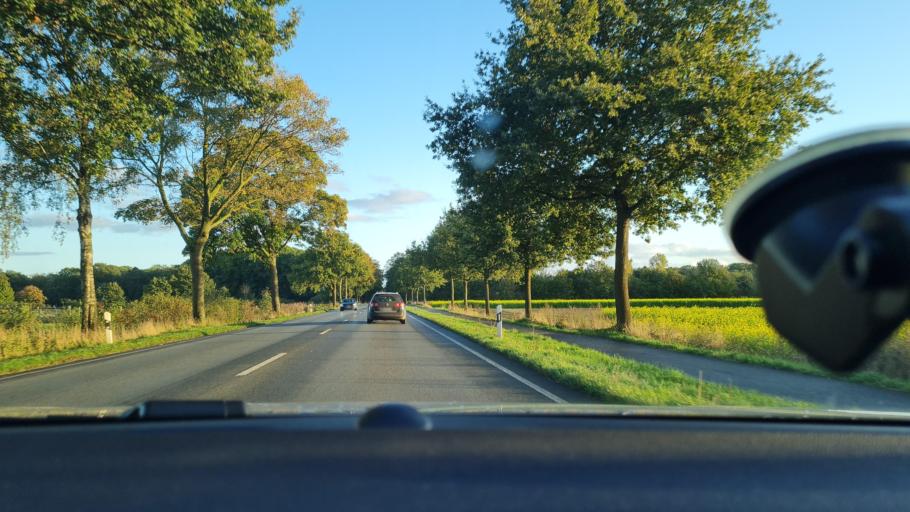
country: DE
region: North Rhine-Westphalia
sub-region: Regierungsbezirk Dusseldorf
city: Voerde
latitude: 51.6104
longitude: 6.6976
